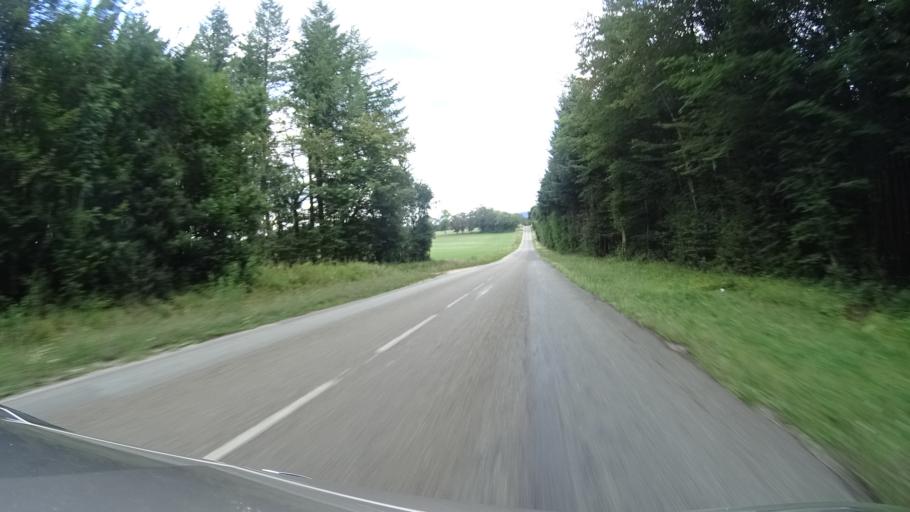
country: FR
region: Franche-Comte
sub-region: Departement du Doubs
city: Mamirolle
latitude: 47.2236
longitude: 6.1482
